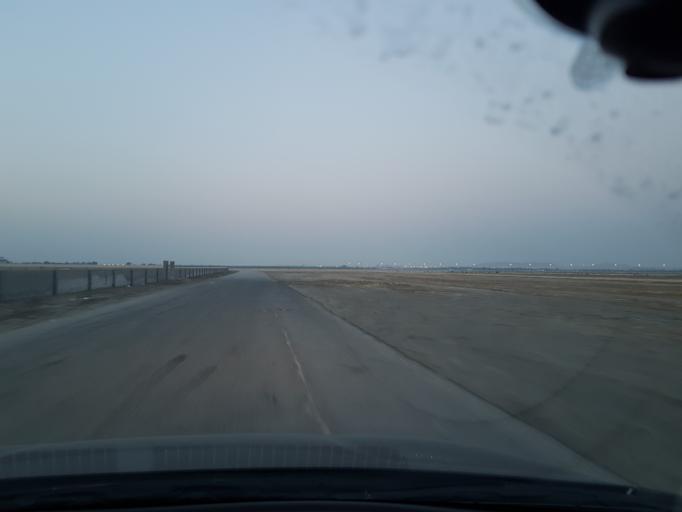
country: BH
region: Central Governorate
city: Dar Kulayb
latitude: 26.0009
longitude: 50.4723
